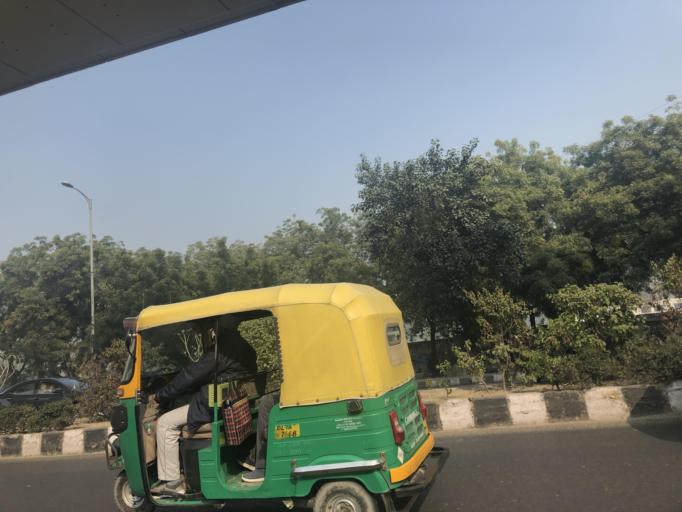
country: IN
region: NCT
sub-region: North West Delhi
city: Pitampura
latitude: 28.6760
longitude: 77.1219
